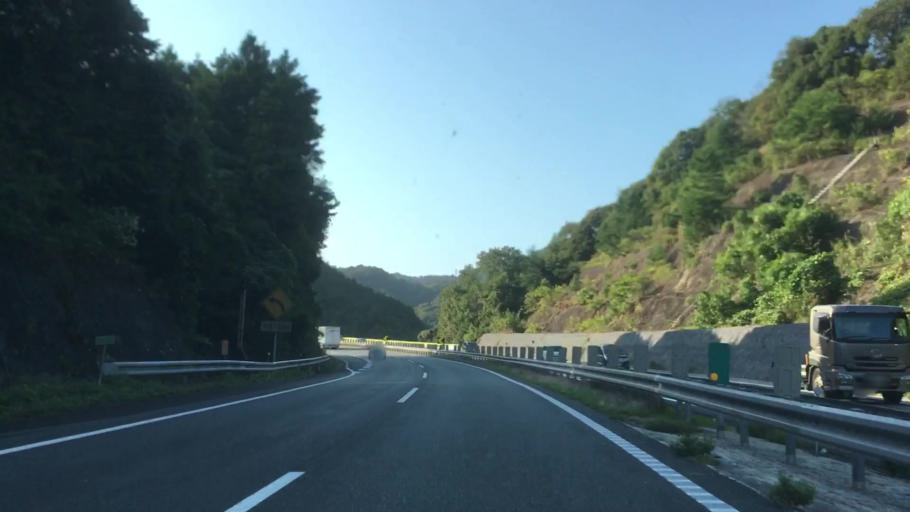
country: JP
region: Yamaguchi
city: Ogori-shimogo
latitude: 34.1355
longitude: 131.3744
